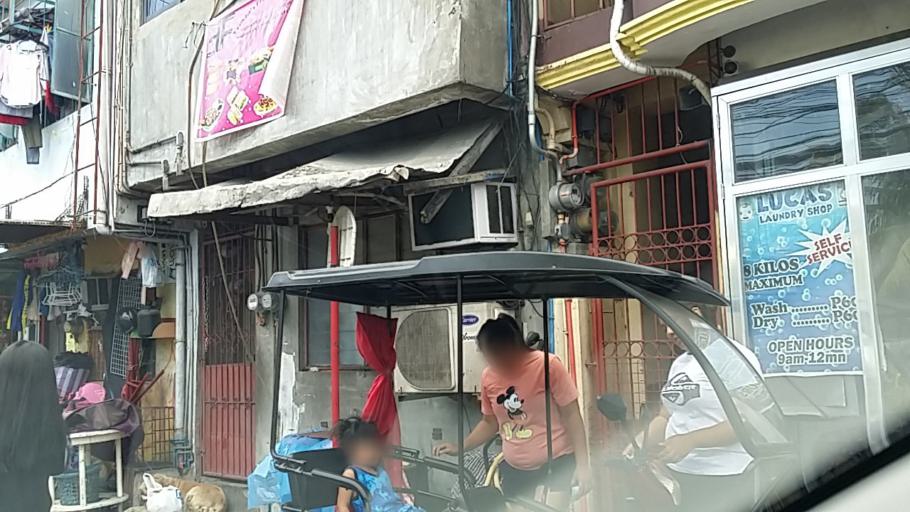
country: PH
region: Metro Manila
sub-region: Mandaluyong
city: Mandaluyong City
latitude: 14.5817
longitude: 121.0463
